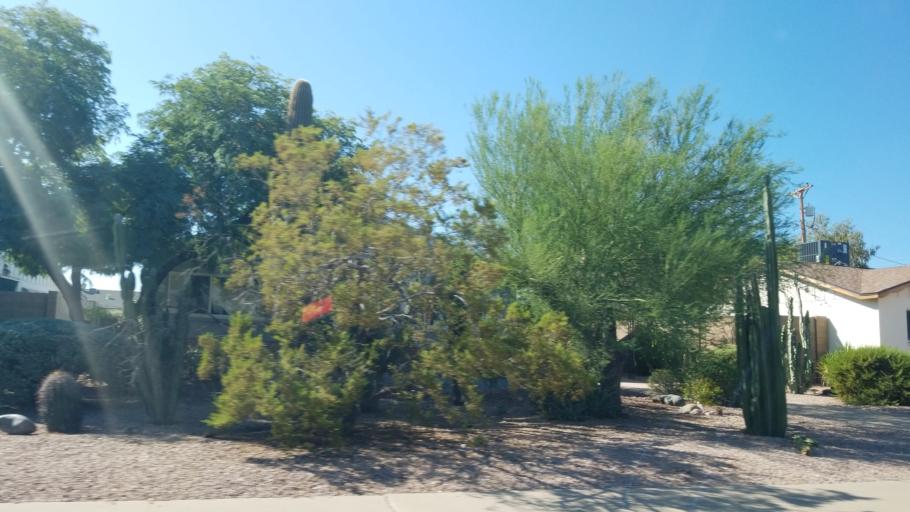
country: US
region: Arizona
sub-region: Maricopa County
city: Tempe Junction
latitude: 33.4583
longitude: -111.9369
